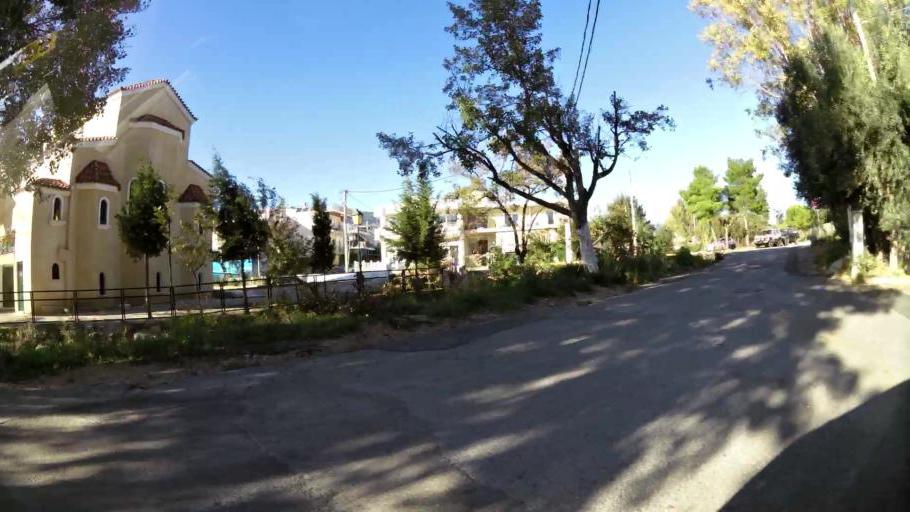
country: GR
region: Attica
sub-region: Nomarchia Anatolikis Attikis
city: Acharnes
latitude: 38.0947
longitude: 23.7370
